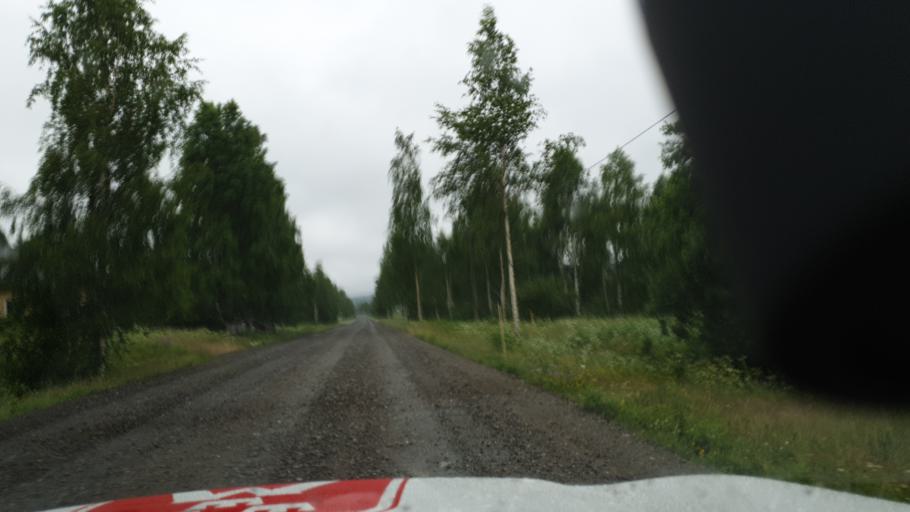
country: SE
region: Vaesterbotten
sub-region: Vannas Kommun
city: Vaennaes
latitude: 63.7493
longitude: 19.6435
